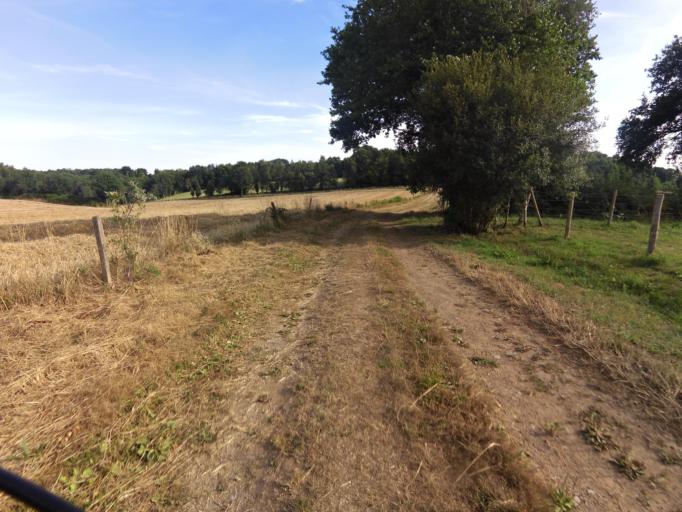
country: FR
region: Brittany
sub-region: Departement du Morbihan
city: Molac
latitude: 47.7042
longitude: -2.4170
